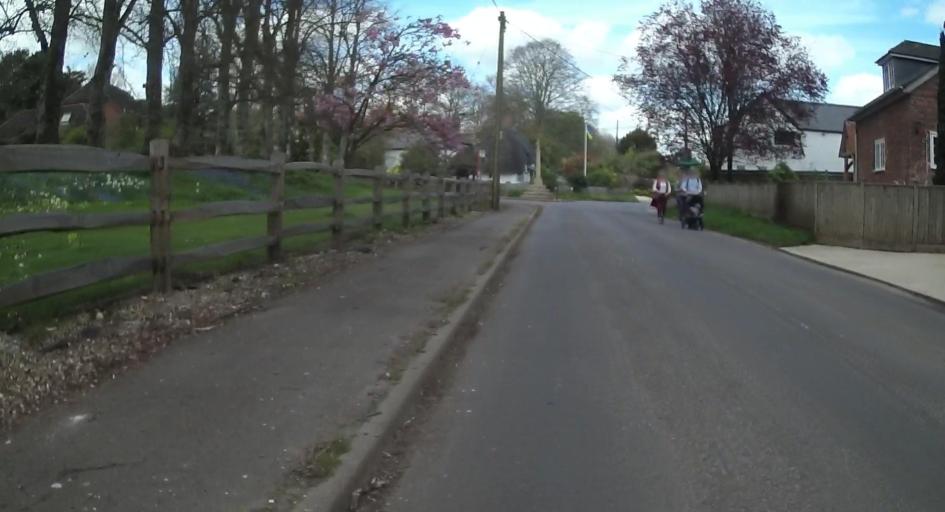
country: GB
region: England
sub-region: Hampshire
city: Abbotts Ann
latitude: 51.0908
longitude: -1.5118
